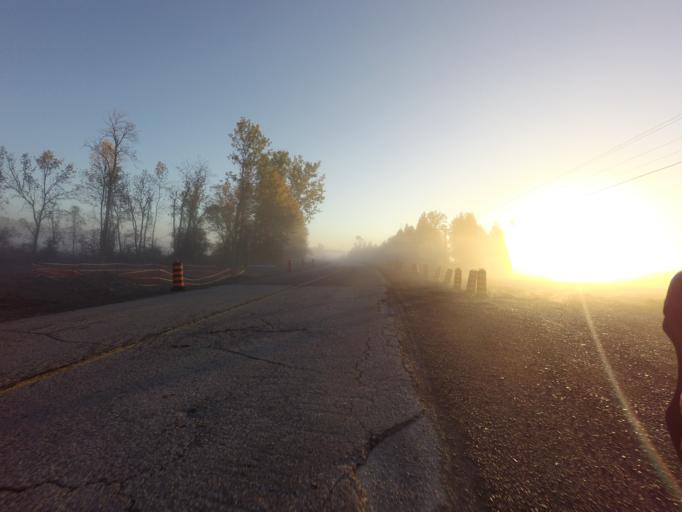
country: CA
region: Ontario
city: Quinte West
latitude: 44.0402
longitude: -77.6068
